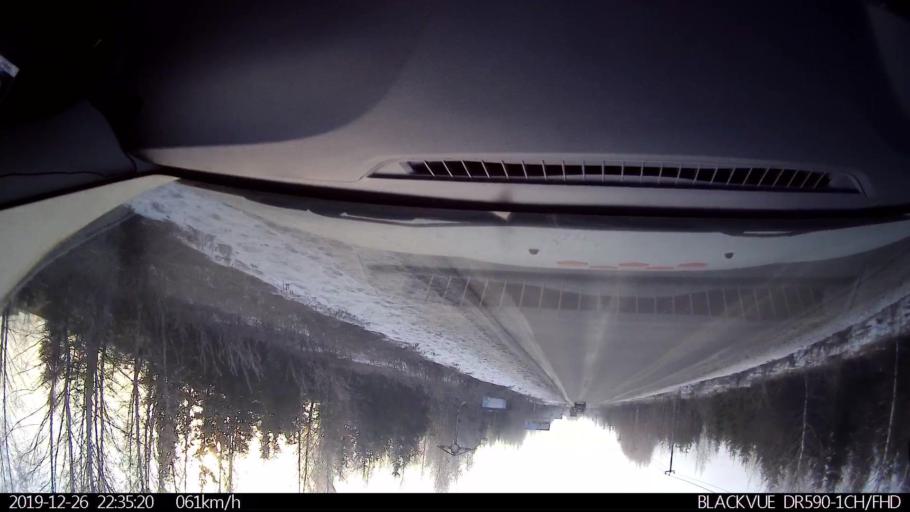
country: RU
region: Nizjnij Novgorod
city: Burevestnik
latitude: 56.1483
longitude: 43.7187
